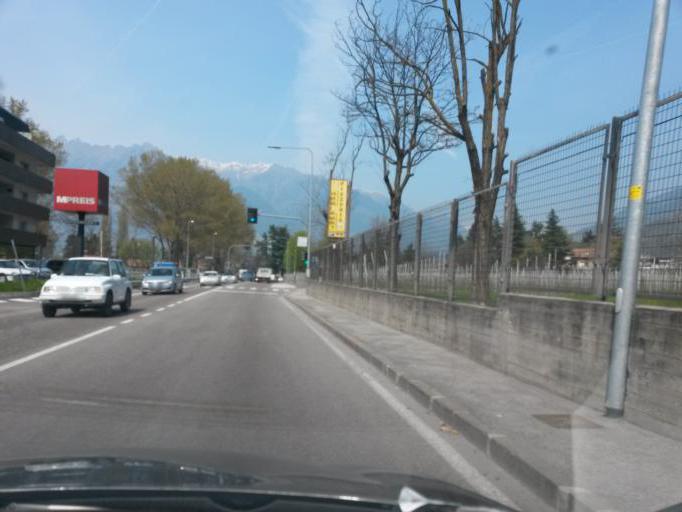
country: IT
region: Trentino-Alto Adige
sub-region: Bolzano
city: Sinigo
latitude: 46.6363
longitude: 11.1762
